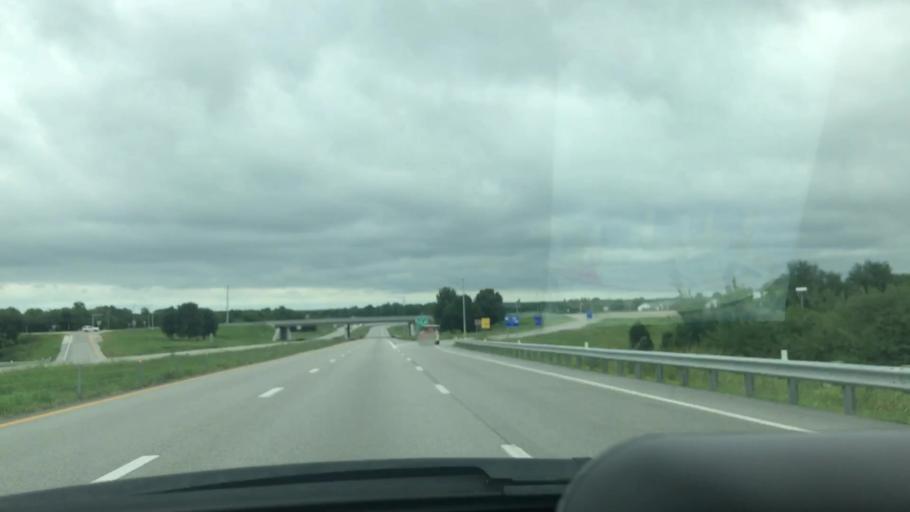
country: US
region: Missouri
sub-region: Greene County
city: Springfield
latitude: 37.2430
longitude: -93.3513
